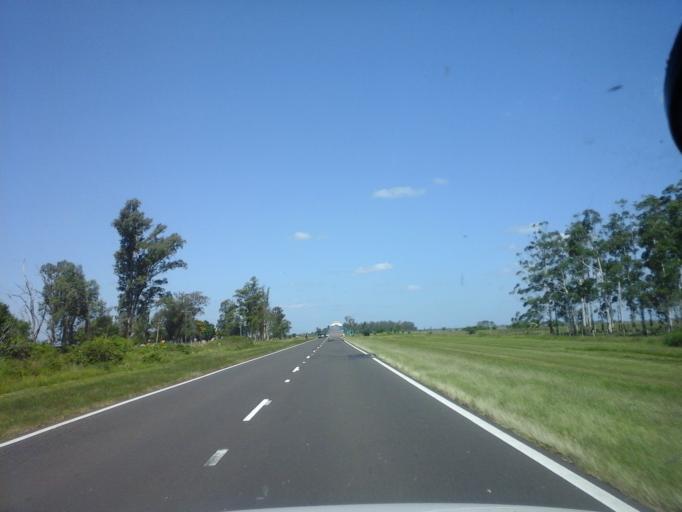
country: PY
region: Neembucu
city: Cerrito
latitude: -27.3863
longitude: -57.7122
